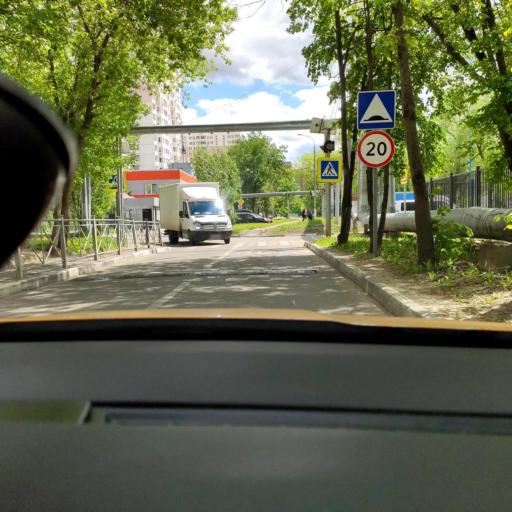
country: RU
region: Moskovskaya
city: Novopodrezkovo
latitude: 55.9421
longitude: 37.3451
